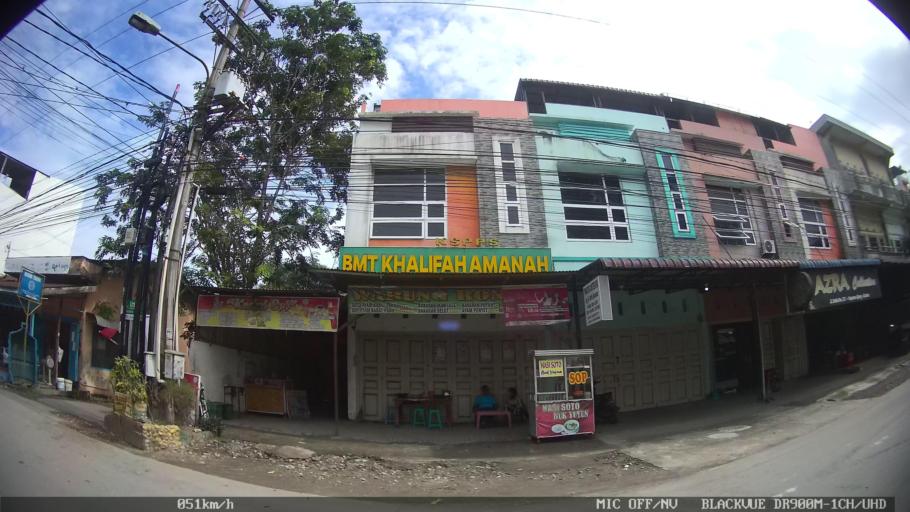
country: ID
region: North Sumatra
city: Sunggal
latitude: 3.6100
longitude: 98.6105
